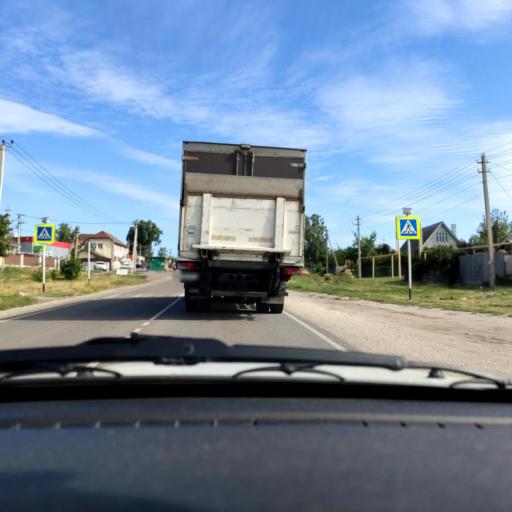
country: RU
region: Voronezj
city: Orlovo
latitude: 51.7510
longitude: 39.5877
